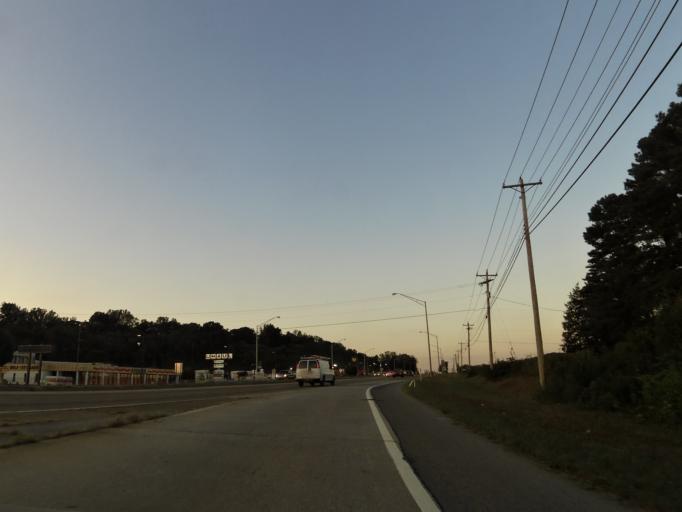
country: US
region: Tennessee
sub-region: Blount County
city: Alcoa
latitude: 35.8380
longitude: -83.9698
